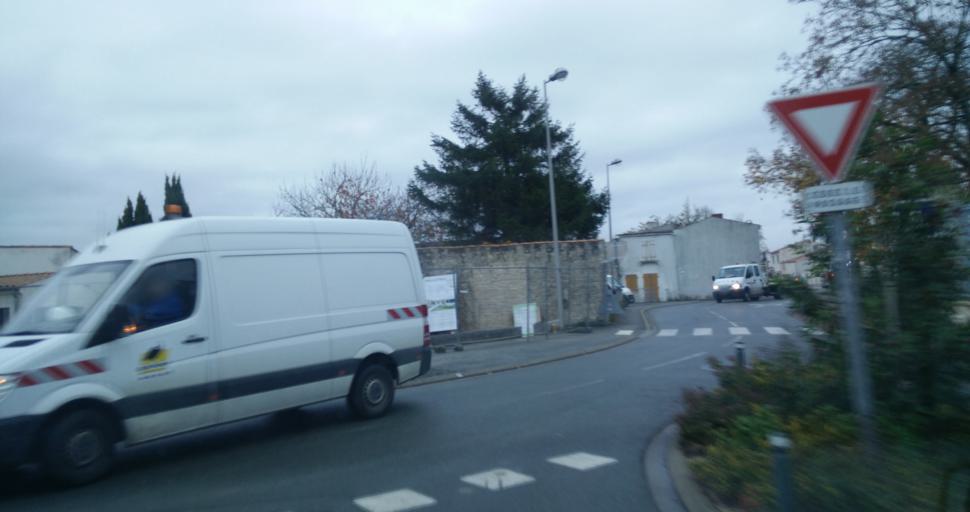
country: FR
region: Poitou-Charentes
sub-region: Departement de la Charente-Maritime
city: Puilboreau
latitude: 46.1881
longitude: -1.1190
